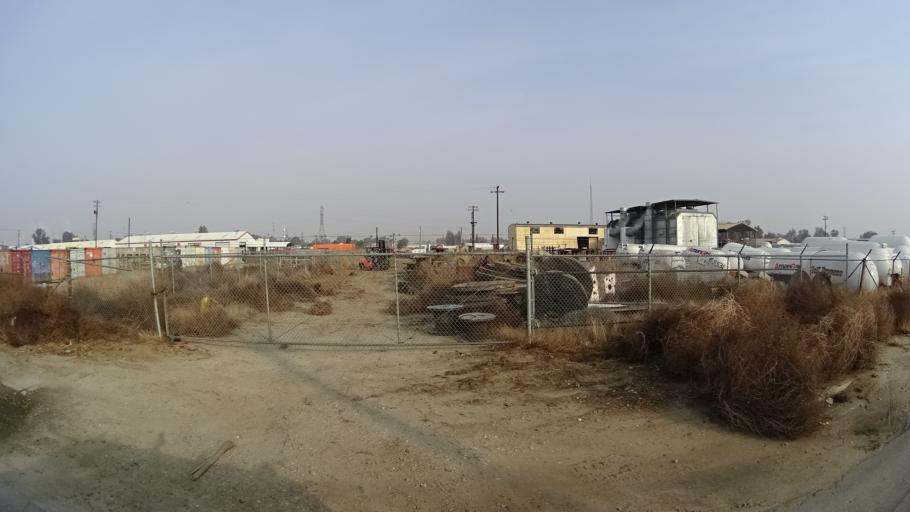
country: US
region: California
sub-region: Kern County
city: Bakersfield
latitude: 35.3939
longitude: -119.0410
